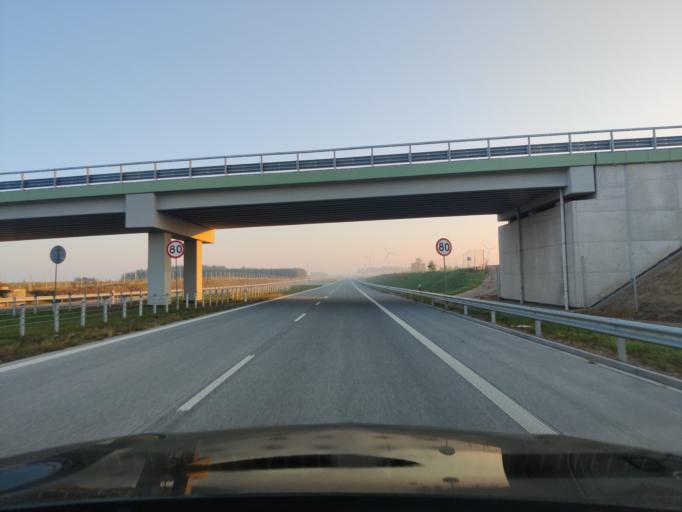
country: PL
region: Masovian Voivodeship
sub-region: Powiat mlawski
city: Wisniewo
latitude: 53.0263
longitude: 20.3464
